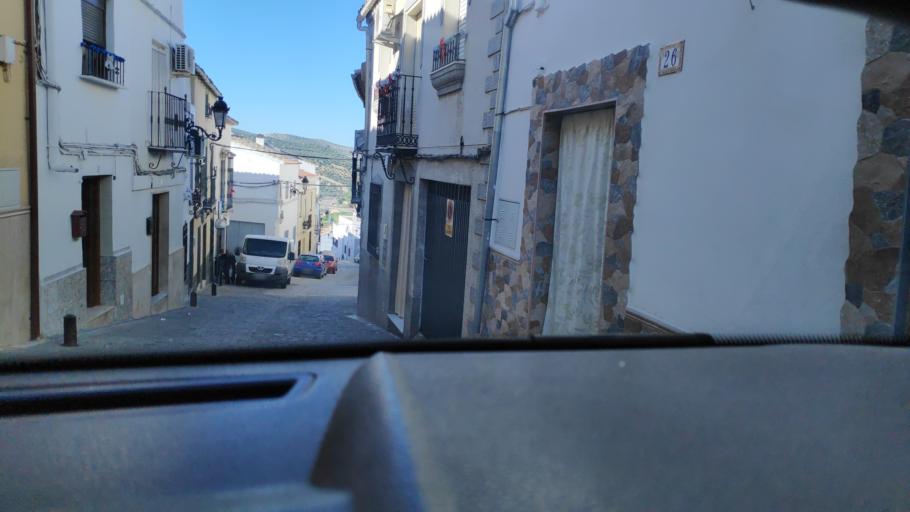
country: ES
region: Andalusia
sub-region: Province of Cordoba
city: Baena
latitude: 37.6140
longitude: -4.3325
